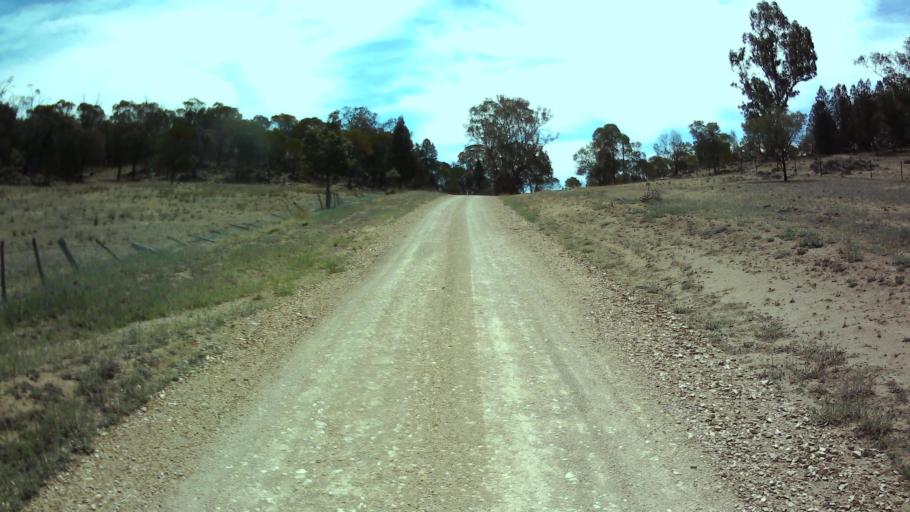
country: AU
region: New South Wales
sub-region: Weddin
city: Grenfell
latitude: -33.7458
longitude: 148.1826
